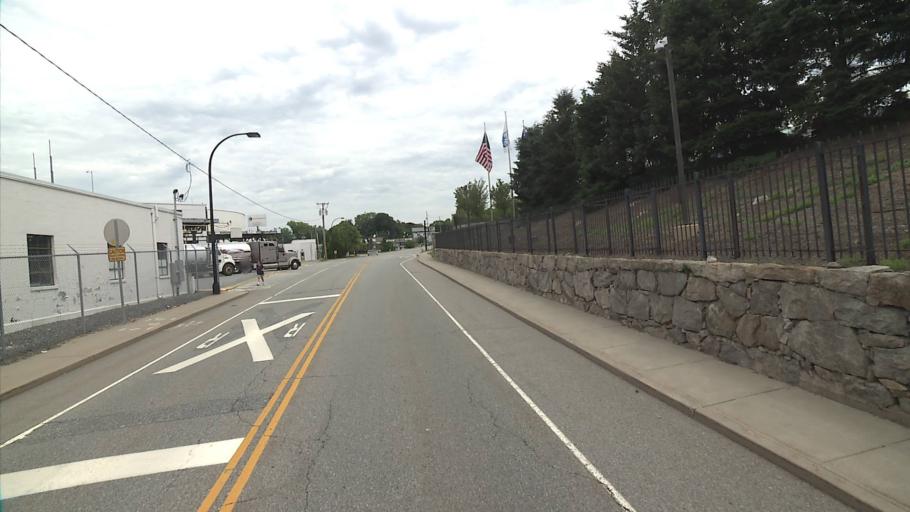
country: US
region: Connecticut
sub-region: New London County
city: Groton
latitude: 41.3355
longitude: -72.0764
